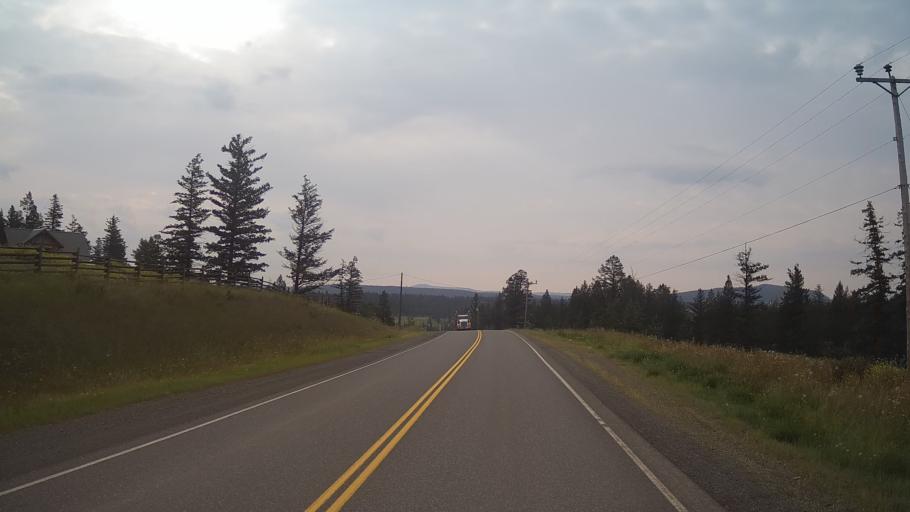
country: CA
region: British Columbia
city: Williams Lake
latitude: 51.9696
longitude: -122.5413
